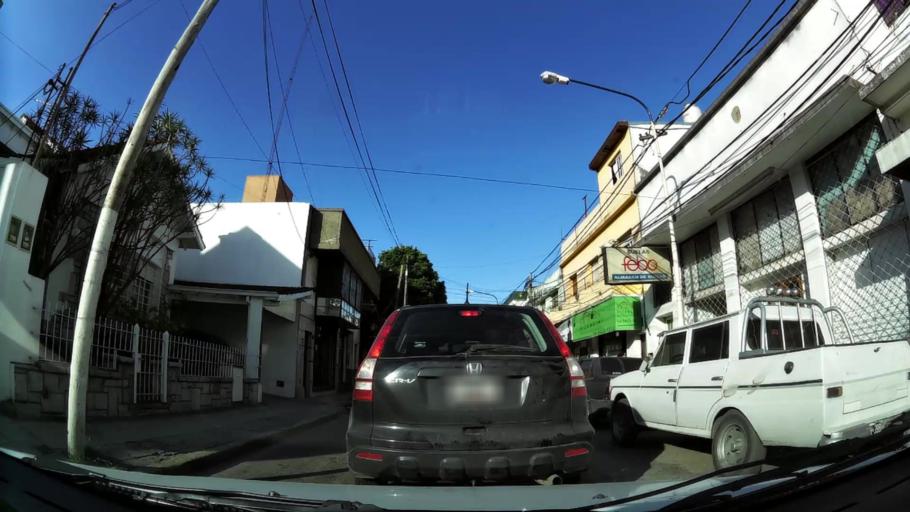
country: AR
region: Buenos Aires
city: Caseros
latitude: -34.5882
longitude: -58.5901
